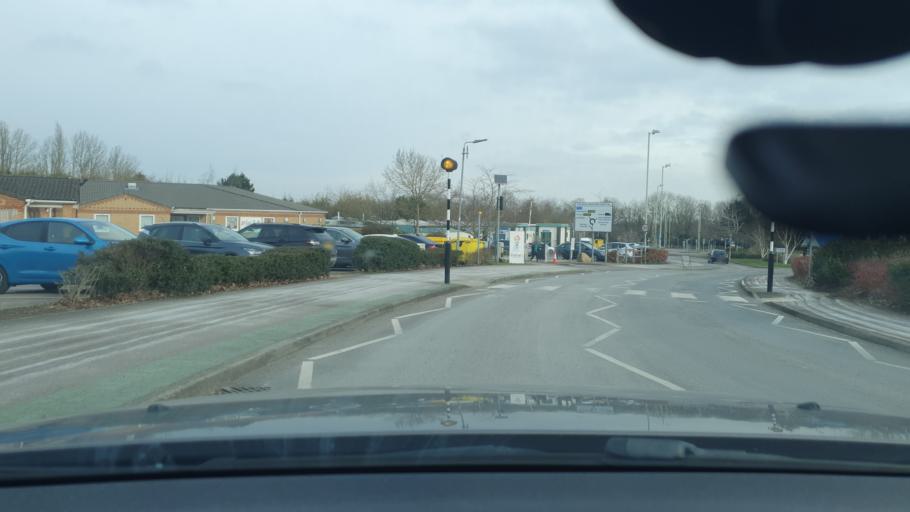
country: GB
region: England
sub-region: Borough of Swindon
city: Chiseldon
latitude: 51.5399
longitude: -1.7296
